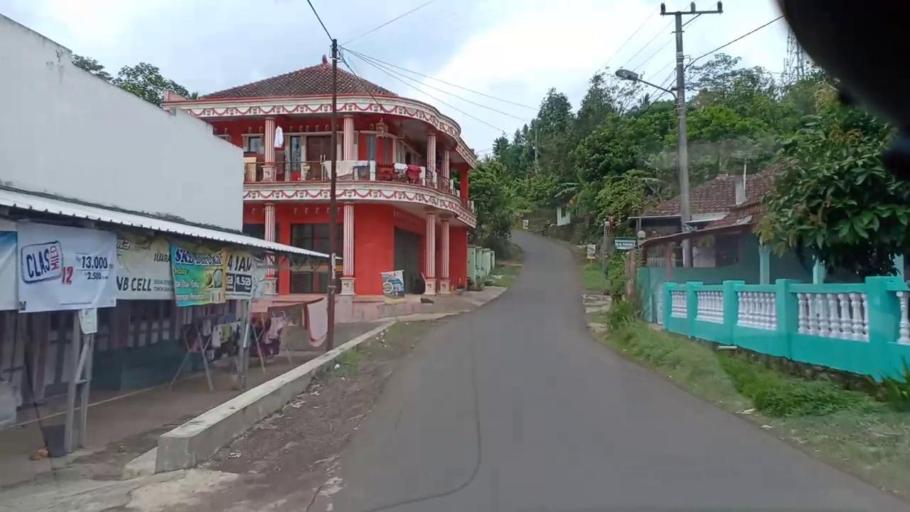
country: ID
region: West Java
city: Gerempay
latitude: -7.3379
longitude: 108.2873
